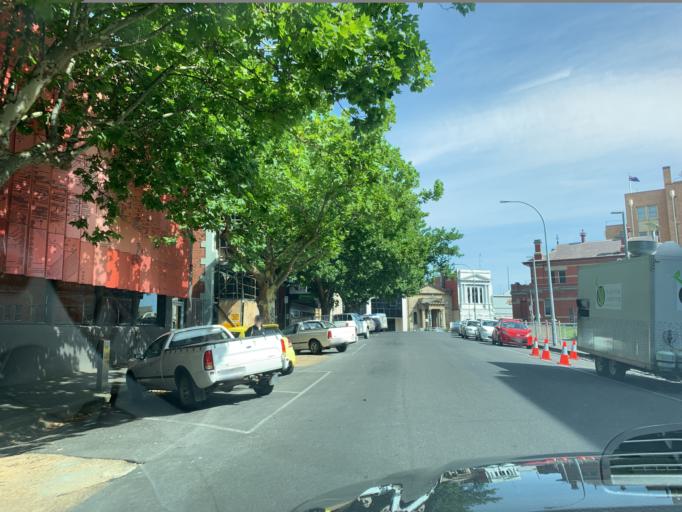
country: AU
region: Victoria
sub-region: Ballarat North
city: Ballarat Central
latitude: -37.5605
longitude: 143.8591
